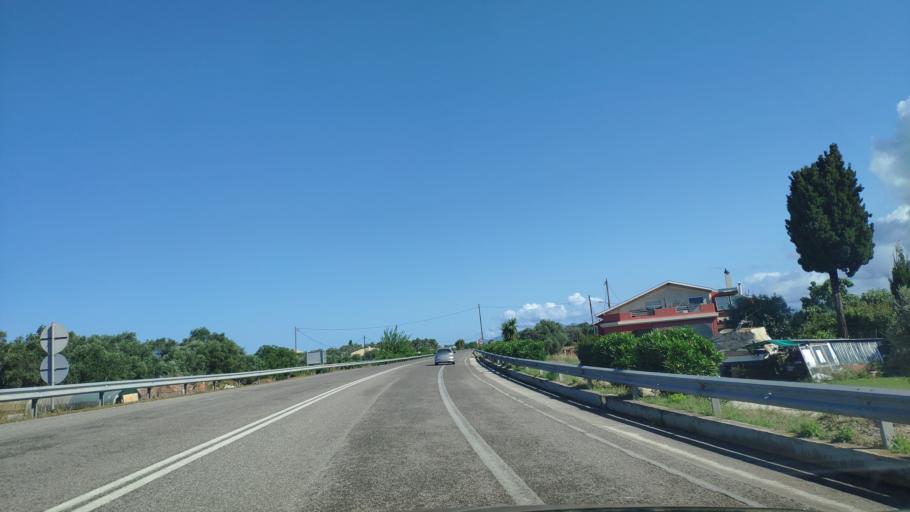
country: GR
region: Epirus
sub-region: Nomos Prevezis
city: Preveza
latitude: 38.9510
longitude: 20.7344
